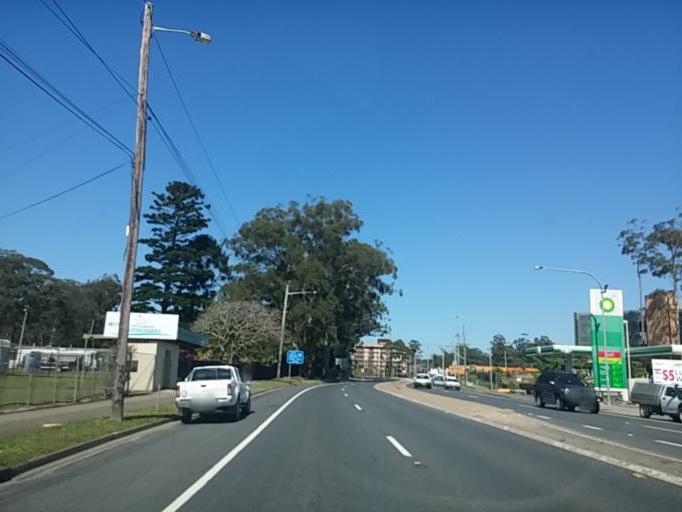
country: AU
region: New South Wales
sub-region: Coffs Harbour
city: Coffs Harbour
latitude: -30.2915
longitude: 153.1192
